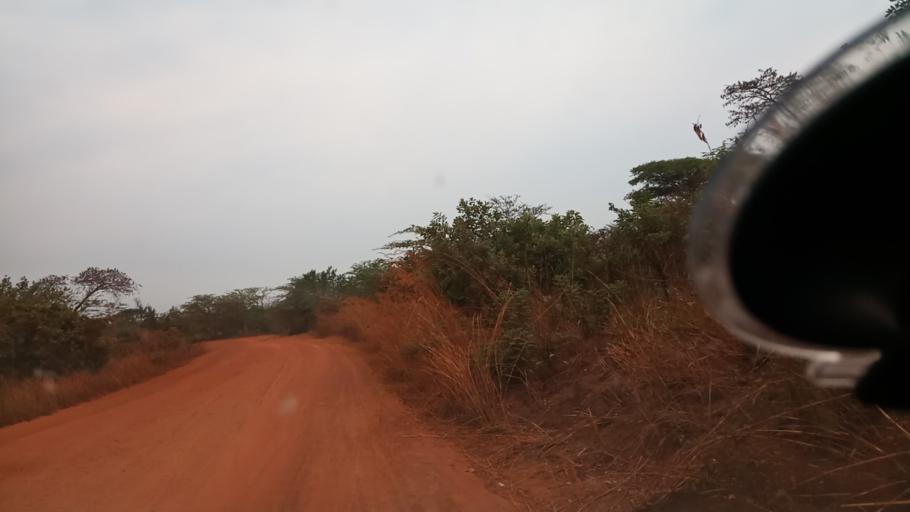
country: ZM
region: Luapula
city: Nchelenge
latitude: -9.1134
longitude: 28.3038
